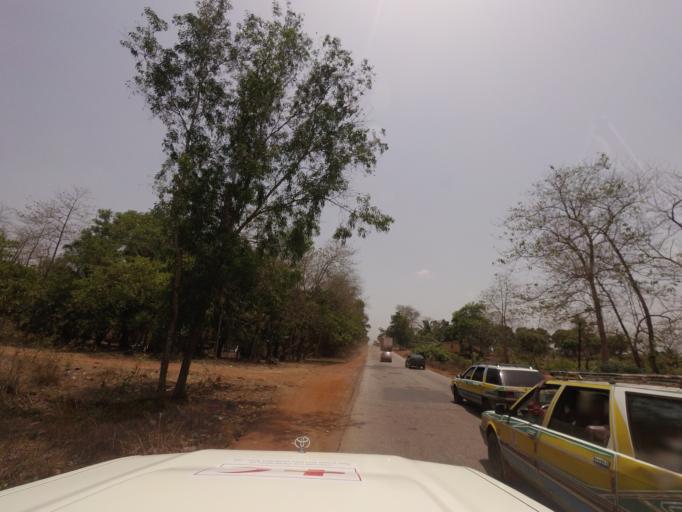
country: GN
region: Kindia
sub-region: Coyah
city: Coyah
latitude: 9.8136
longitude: -13.2688
